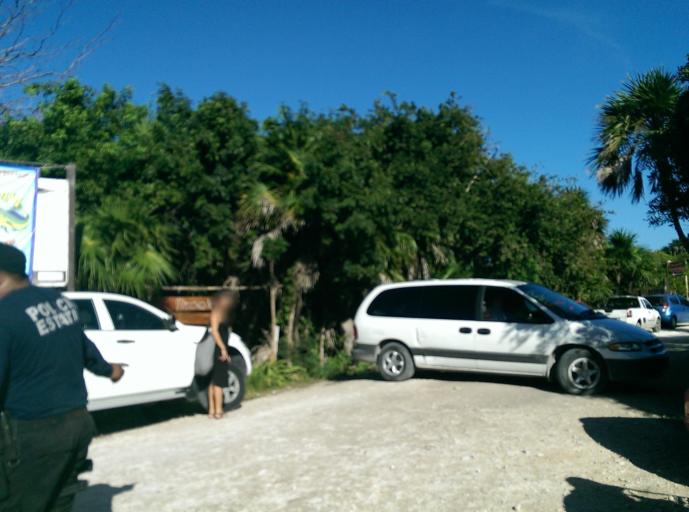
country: MX
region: Quintana Roo
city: Tulum
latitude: 20.2033
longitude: -87.4343
